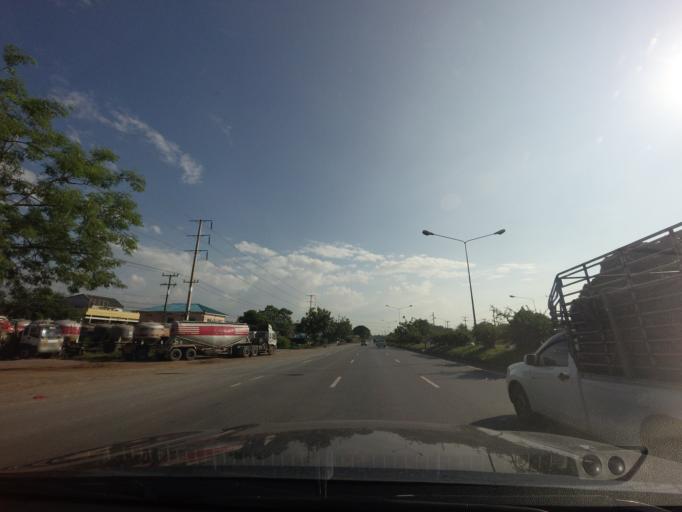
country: TH
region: Sara Buri
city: Chaloem Phra Kiat
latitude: 14.6594
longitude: 100.8862
